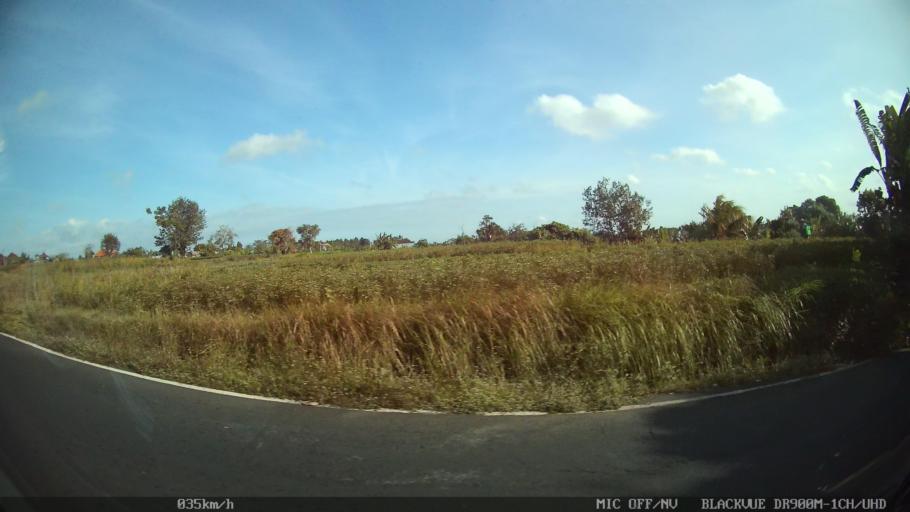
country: ID
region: Bali
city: Banjar Desa
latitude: -8.5797
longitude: 115.2294
